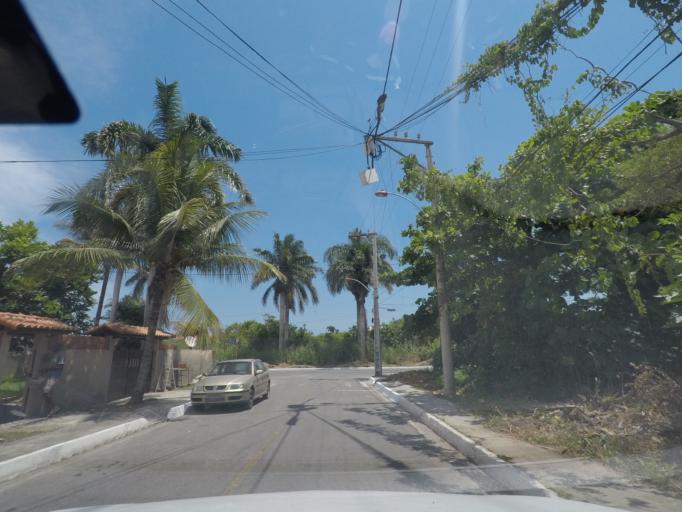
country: BR
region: Rio de Janeiro
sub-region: Marica
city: Marica
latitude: -22.9674
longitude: -42.9693
